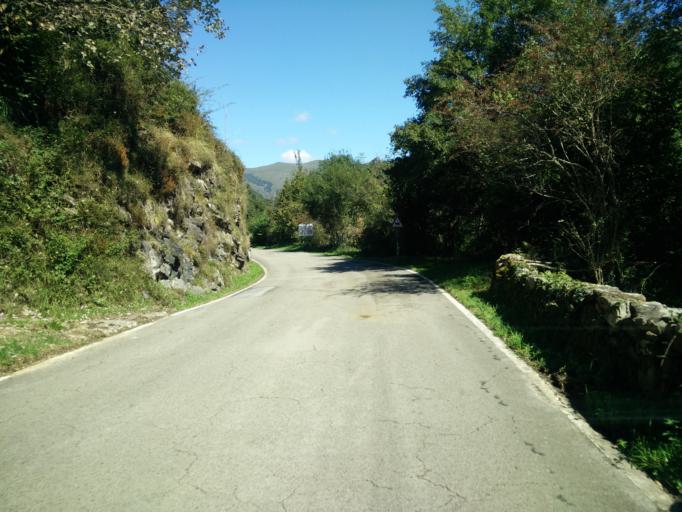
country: ES
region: Cantabria
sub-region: Provincia de Cantabria
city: Ruente
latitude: 43.1395
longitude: -4.2906
